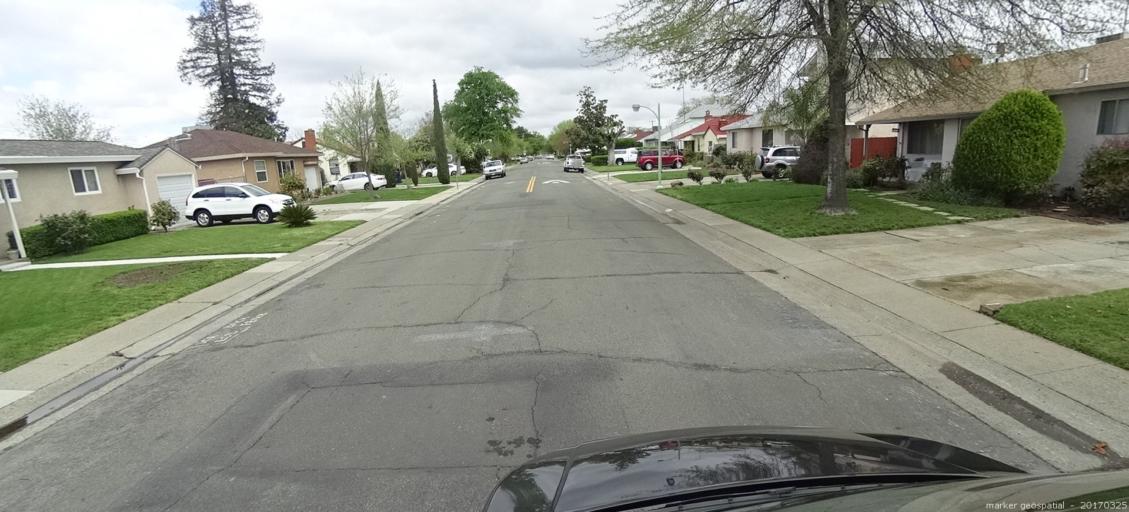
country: US
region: California
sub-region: Sacramento County
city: Florin
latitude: 38.5225
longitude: -121.4328
